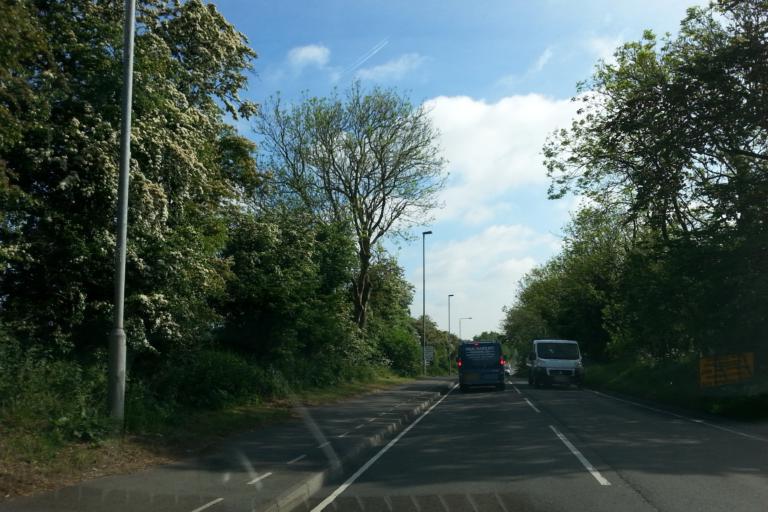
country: GB
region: England
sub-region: Nottinghamshire
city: Mansfield
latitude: 53.1283
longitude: -1.2237
